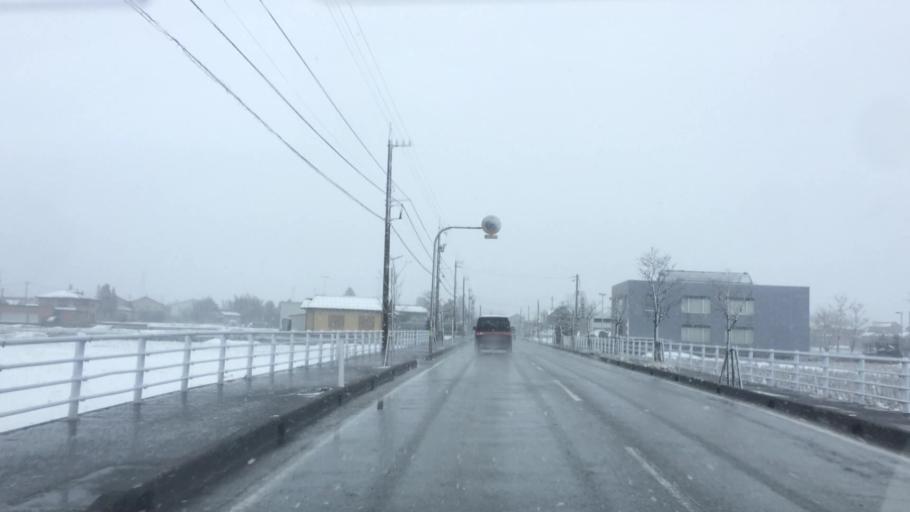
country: JP
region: Toyama
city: Toyama-shi
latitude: 36.6314
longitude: 137.2141
